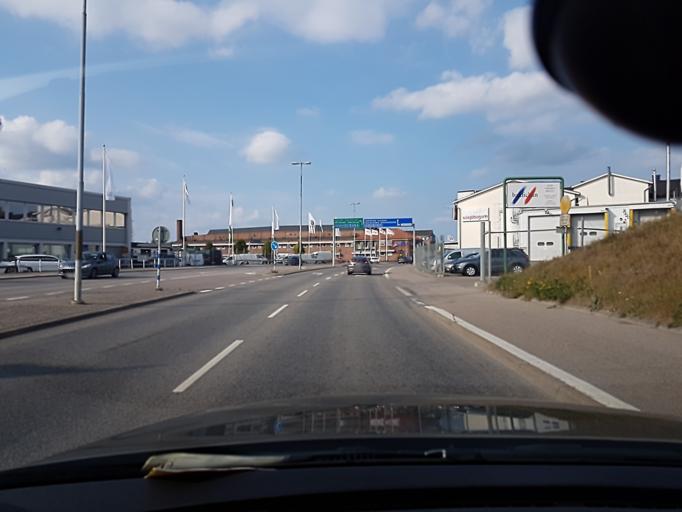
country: SE
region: Kronoberg
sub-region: Vaxjo Kommun
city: Vaexjoe
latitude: 56.8777
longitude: 14.7858
